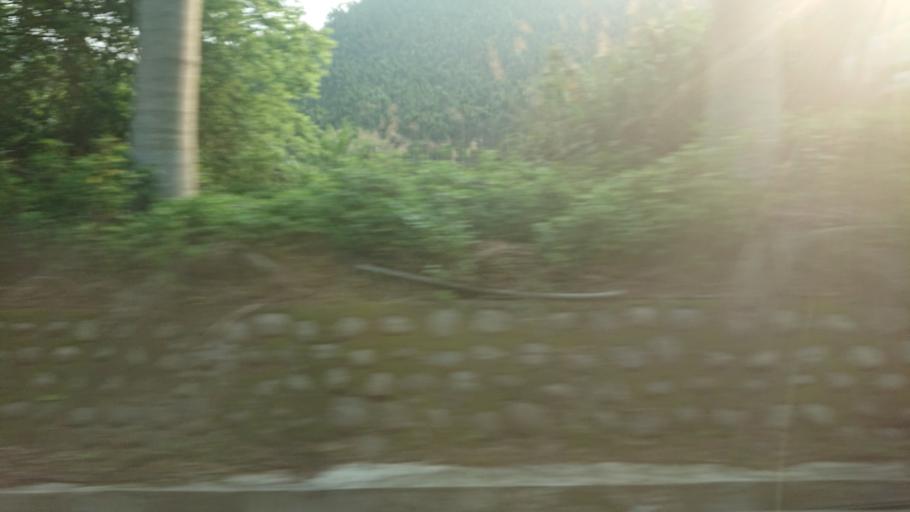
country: TW
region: Taiwan
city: Daxi
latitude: 24.8667
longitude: 121.4155
